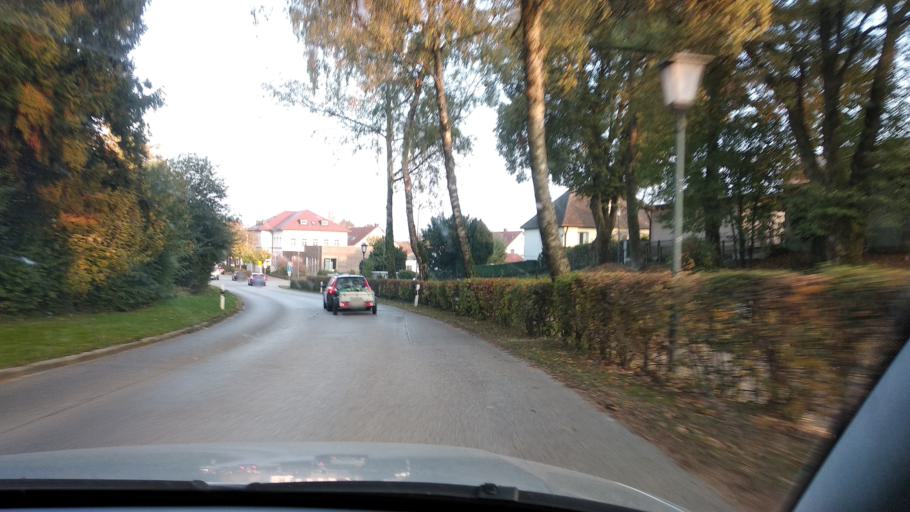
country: DE
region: Bavaria
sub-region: Upper Bavaria
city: Anzing
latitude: 48.1546
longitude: 11.8508
